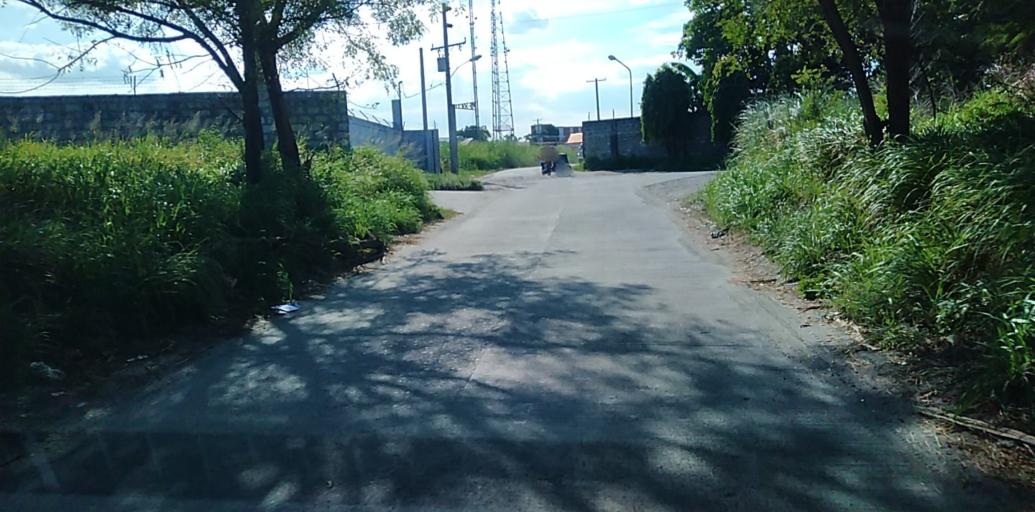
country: PH
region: Central Luzon
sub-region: Province of Pampanga
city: Acli
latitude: 15.1165
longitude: 120.6419
